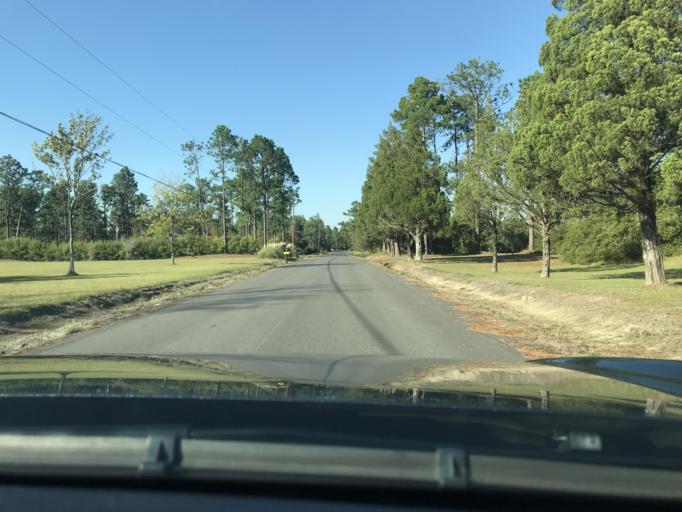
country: US
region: Louisiana
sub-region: Calcasieu Parish
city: Westlake
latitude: 30.3180
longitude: -93.2688
